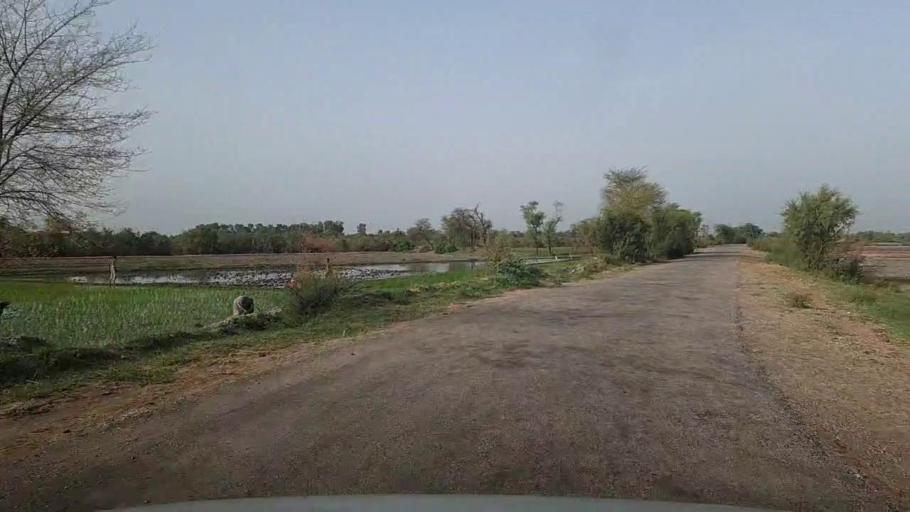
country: PK
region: Sindh
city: Khairpur Nathan Shah
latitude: 27.0883
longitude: 67.7952
